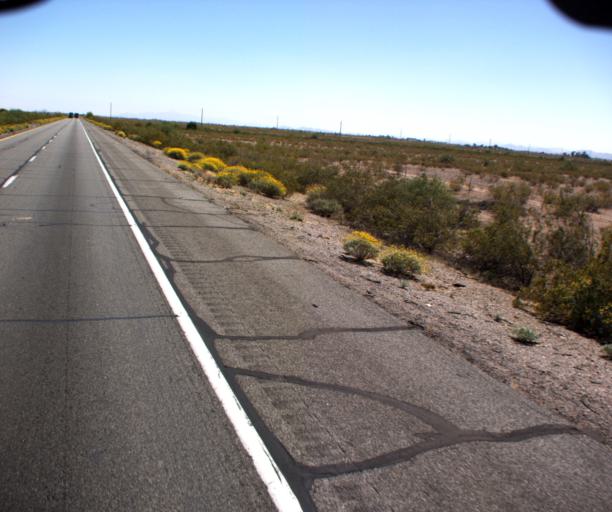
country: US
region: Arizona
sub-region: Maricopa County
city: Buckeye
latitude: 33.4754
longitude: -112.8392
